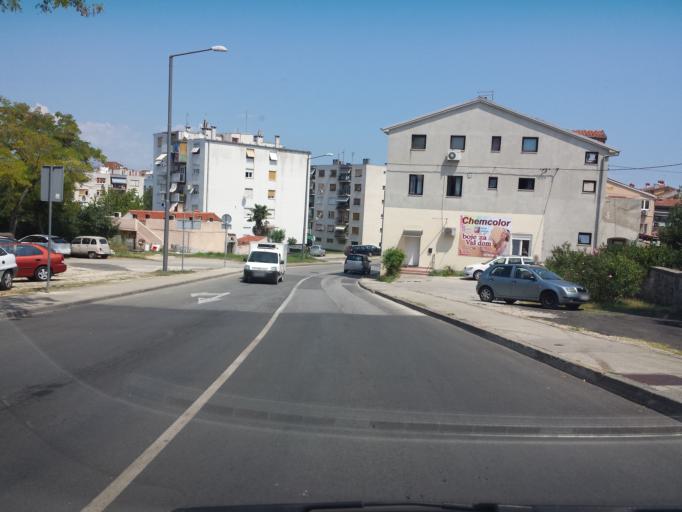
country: HR
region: Istarska
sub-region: Grad Pula
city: Pula
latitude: 44.8747
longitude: 13.8551
